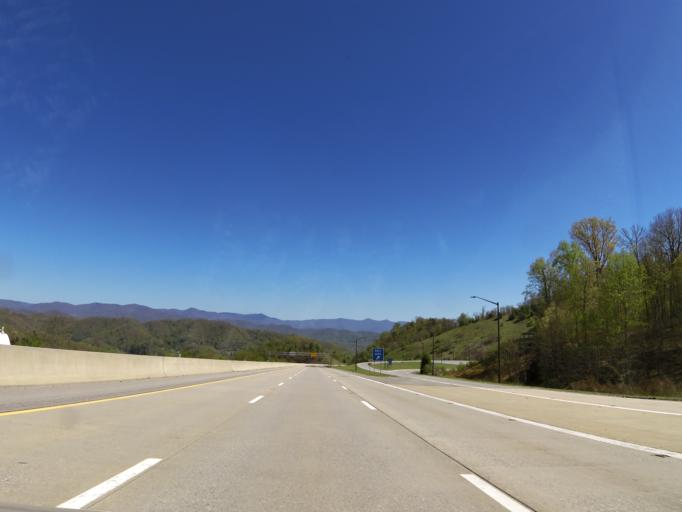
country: US
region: North Carolina
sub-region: Madison County
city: Mars Hill
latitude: 35.8763
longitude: -82.5454
